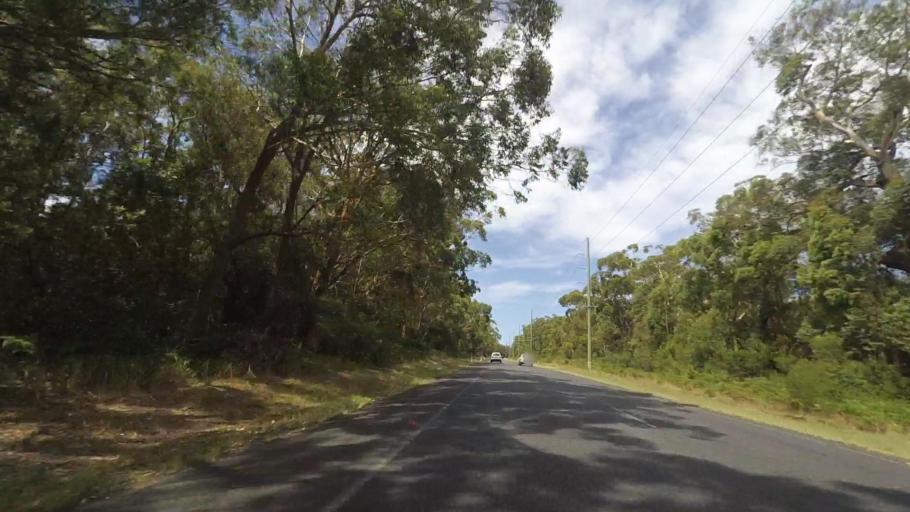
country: AU
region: New South Wales
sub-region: Port Stephens Shire
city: Anna Bay
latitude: -32.7832
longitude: 151.9803
